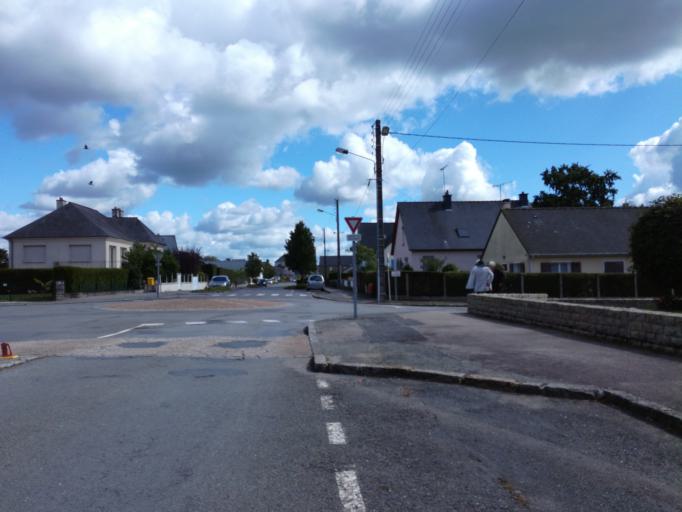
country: FR
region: Brittany
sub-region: Departement d'Ille-et-Vilaine
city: Saint-Aubin-du-Cormier
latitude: 48.2578
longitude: -1.4007
